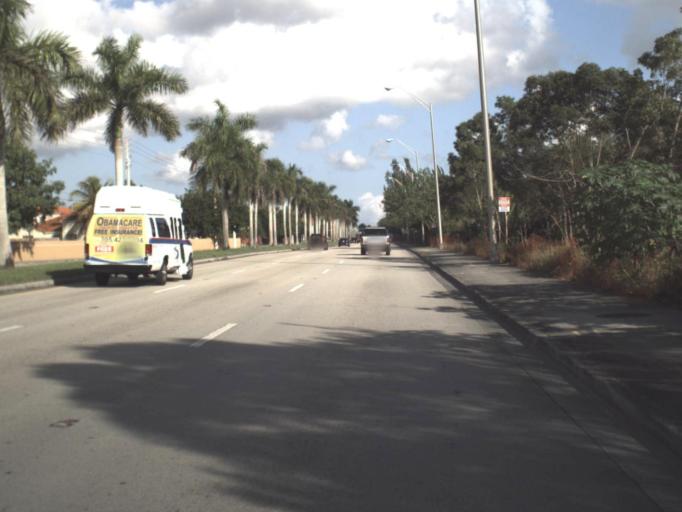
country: US
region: Florida
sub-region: Miami-Dade County
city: Three Lakes
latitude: 25.6266
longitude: -80.3997
